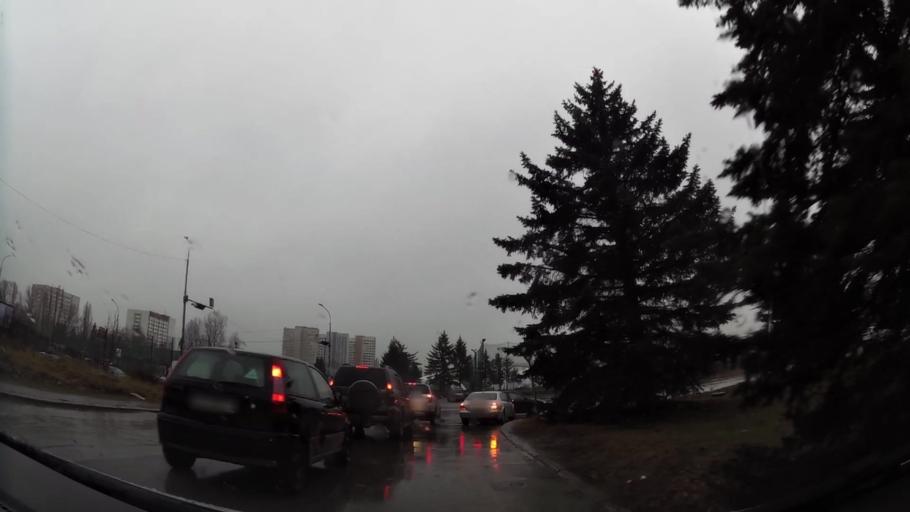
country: BG
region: Sofia-Capital
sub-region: Stolichna Obshtina
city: Sofia
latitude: 42.6519
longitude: 23.3533
